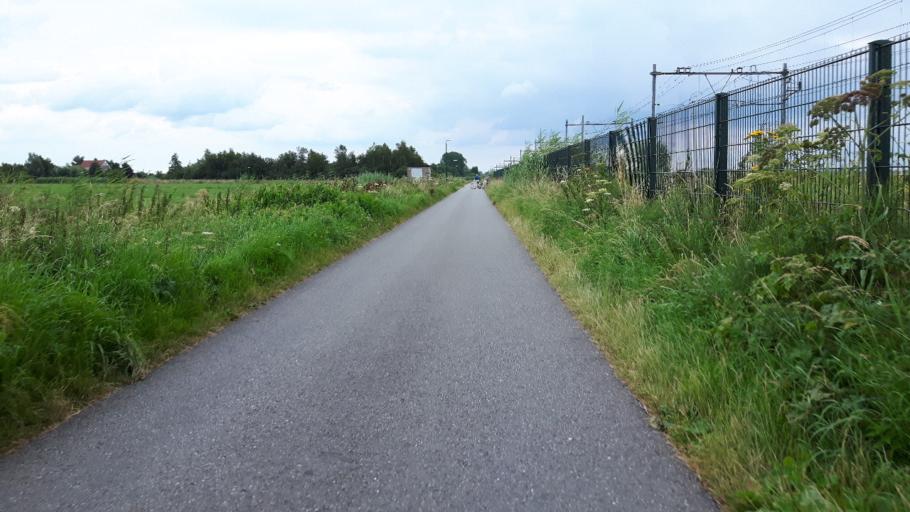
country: NL
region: Utrecht
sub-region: Gemeente Oudewater
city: Oudewater
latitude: 52.0342
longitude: 4.8259
